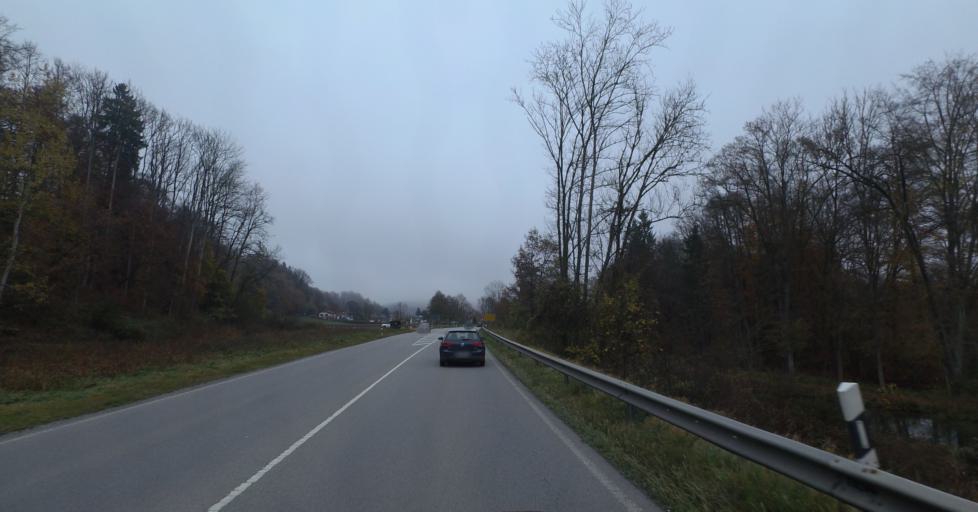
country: DE
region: Bavaria
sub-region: Upper Bavaria
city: Trostberg an der Alz
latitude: 48.0138
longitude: 12.5317
